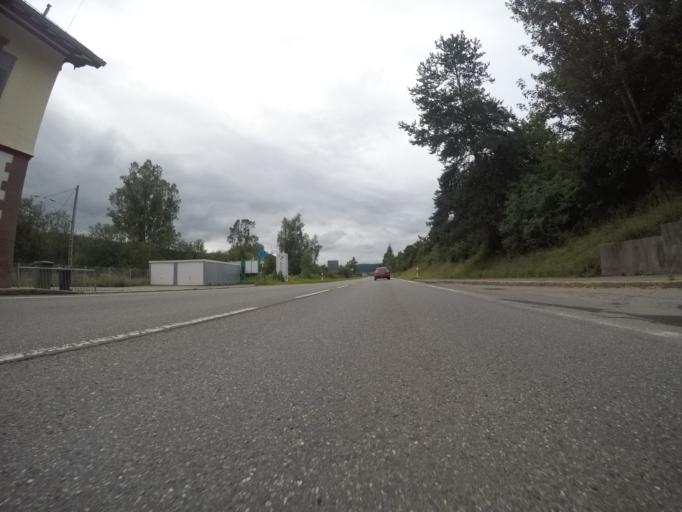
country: DE
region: Baden-Wuerttemberg
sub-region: Freiburg Region
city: Konigsfeld im Schwarzwald
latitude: 48.1238
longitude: 8.3884
